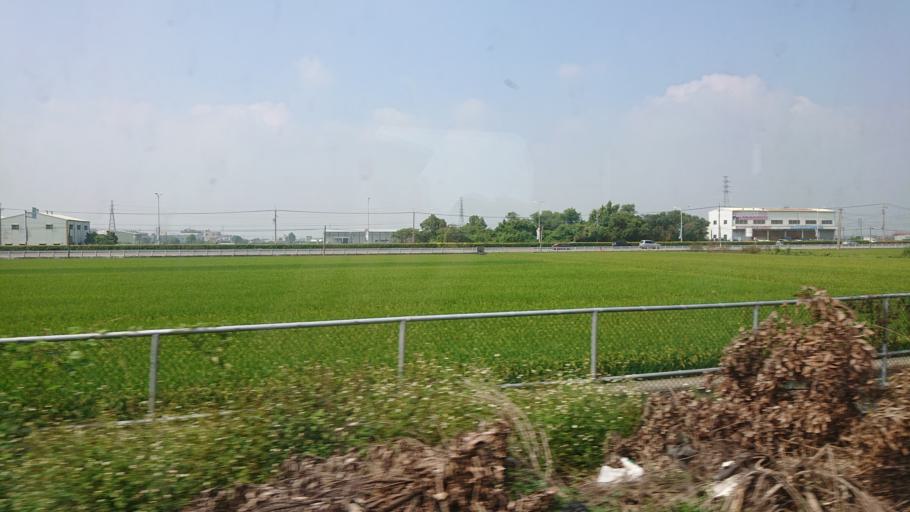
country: TW
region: Taiwan
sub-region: Yunlin
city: Douliu
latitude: 23.6438
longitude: 120.4716
